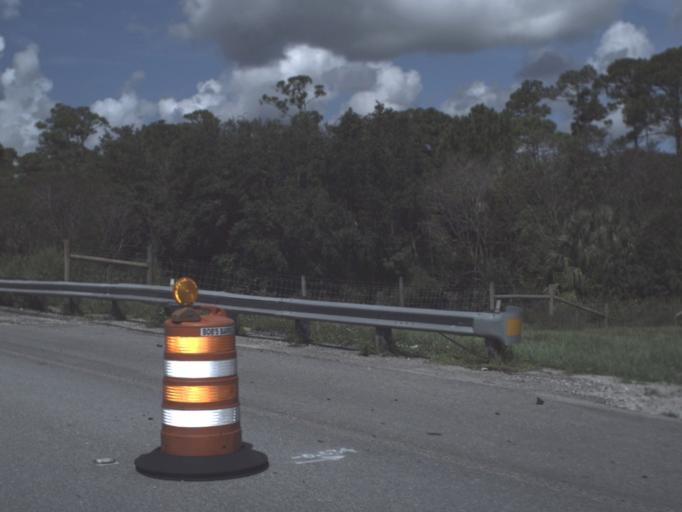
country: US
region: Florida
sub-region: Sarasota County
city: Warm Mineral Springs
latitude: 27.1002
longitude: -82.2708
